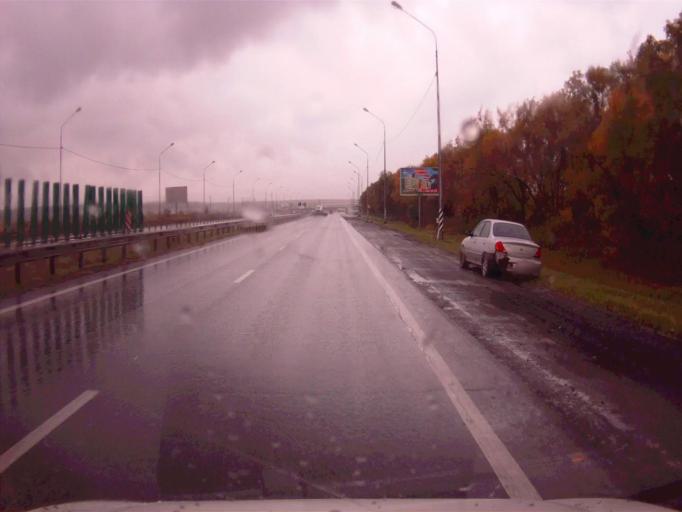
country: RU
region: Chelyabinsk
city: Dolgoderevenskoye
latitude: 55.3049
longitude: 61.3359
